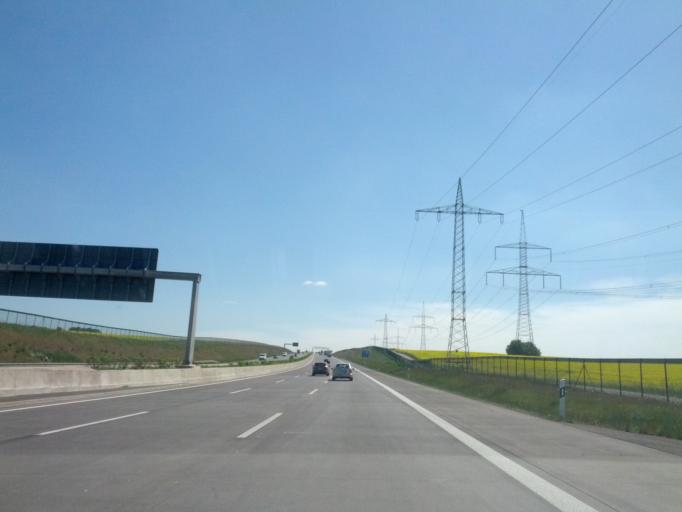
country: DE
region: Thuringia
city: Bischofroda
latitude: 50.9972
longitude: 10.4170
